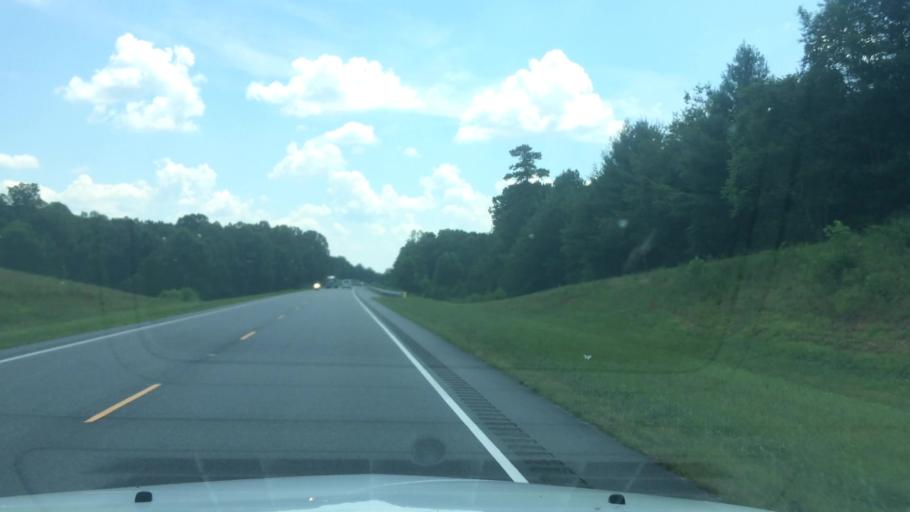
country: US
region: North Carolina
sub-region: Alexander County
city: Stony Point
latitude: 35.8761
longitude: -81.0689
